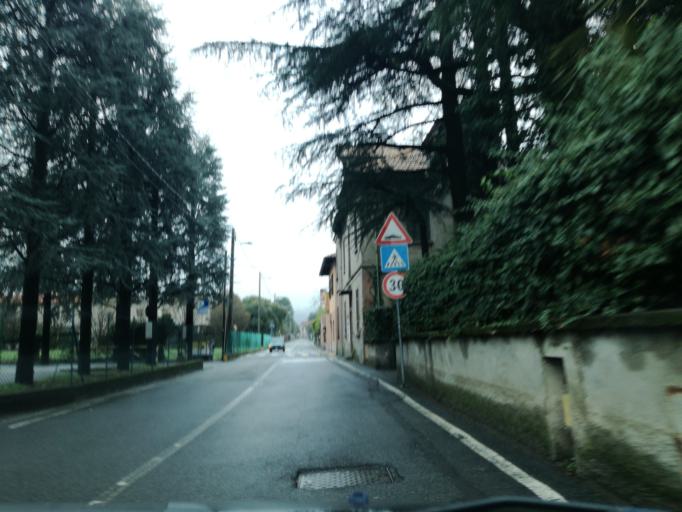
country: IT
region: Lombardy
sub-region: Provincia di Lecco
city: Paderno d'Adda
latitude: 45.6768
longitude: 9.4438
